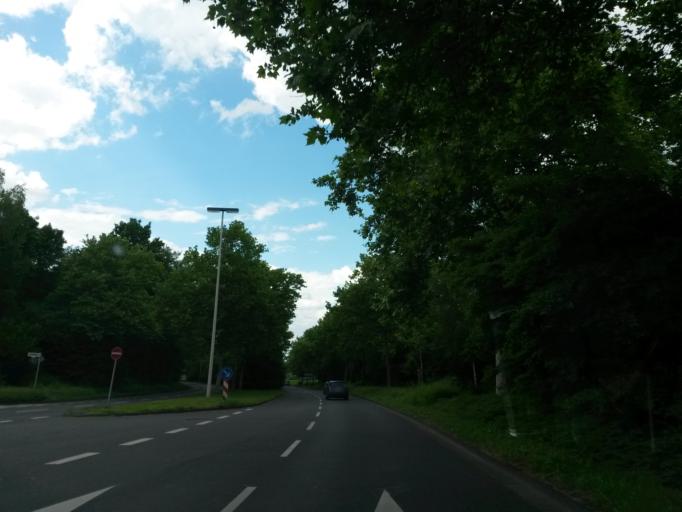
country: DE
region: North Rhine-Westphalia
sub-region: Regierungsbezirk Koln
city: Bonn
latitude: 50.7014
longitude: 7.0601
